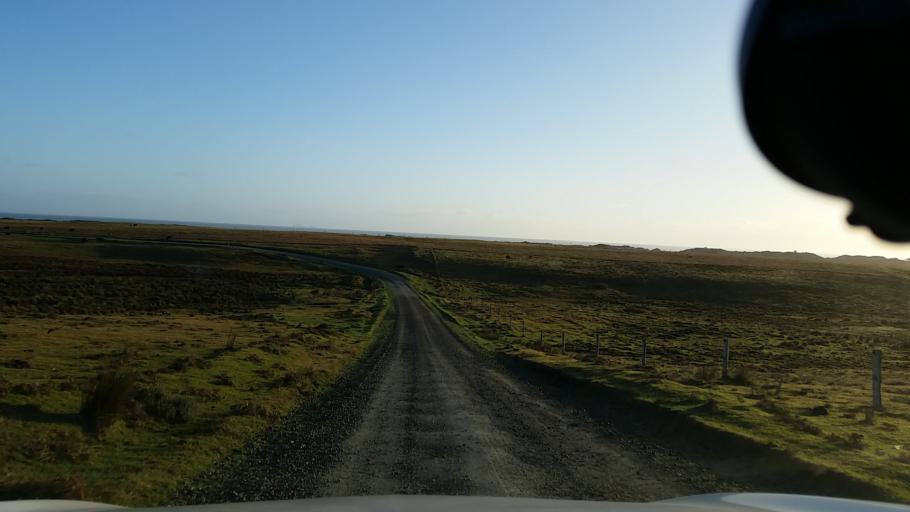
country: NZ
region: Chatham Islands
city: Waitangi
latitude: -43.7752
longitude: -176.7369
